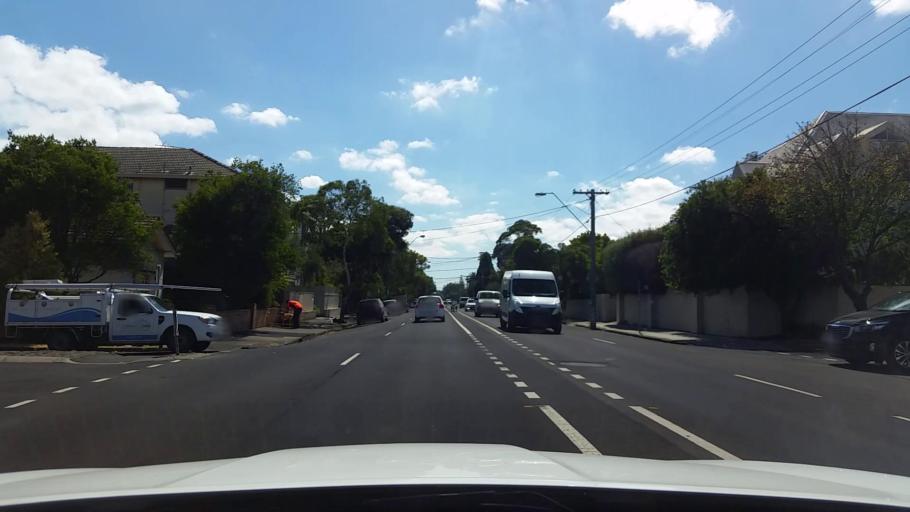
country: AU
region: Victoria
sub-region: Port Phillip
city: Balaclava
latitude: -37.8738
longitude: 144.9986
